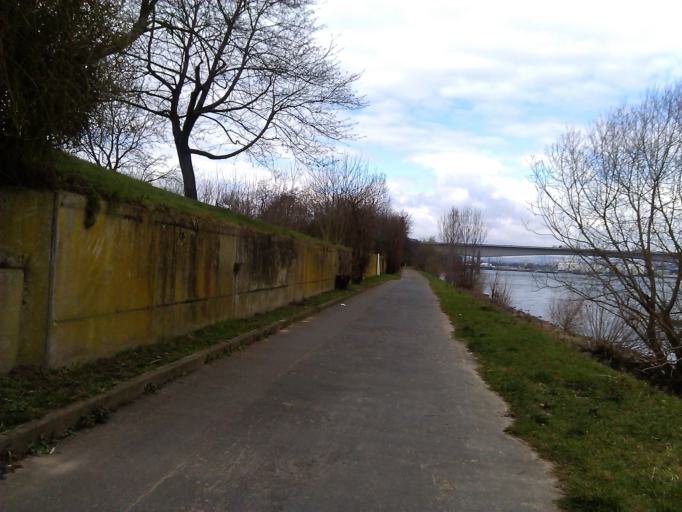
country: DE
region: Rheinland-Pfalz
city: Sankt Sebastian
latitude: 50.4037
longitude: 7.5770
